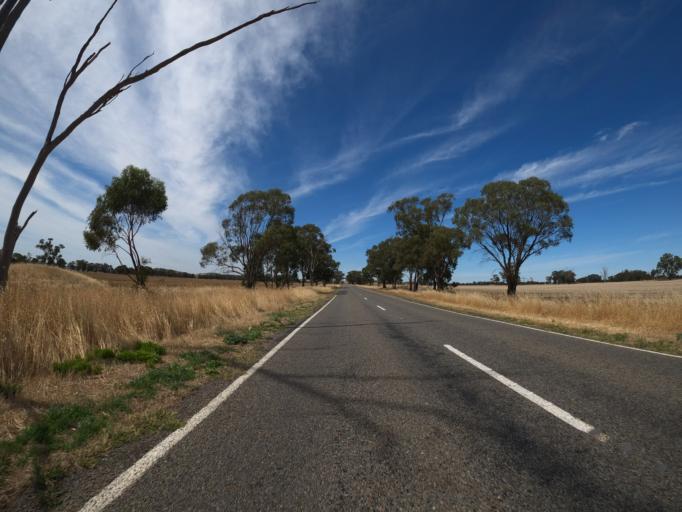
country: AU
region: Victoria
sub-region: Benalla
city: Benalla
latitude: -36.2952
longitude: 145.9523
